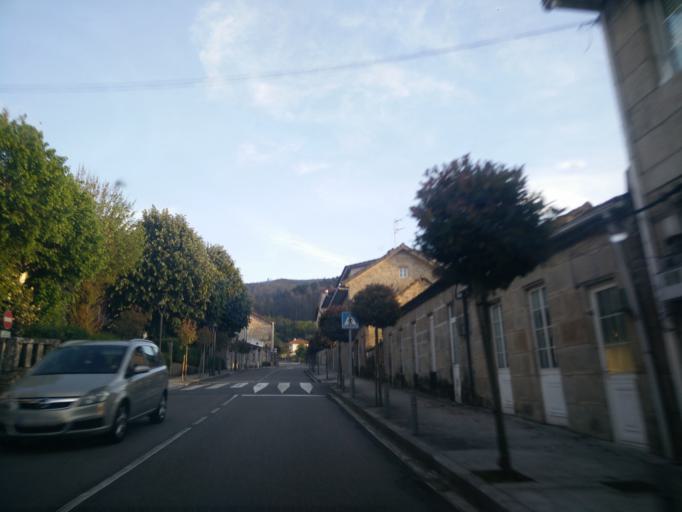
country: ES
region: Galicia
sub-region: Provincia de Pontevedra
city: Mondariz-Balneario
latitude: 42.2261
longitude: -8.4699
